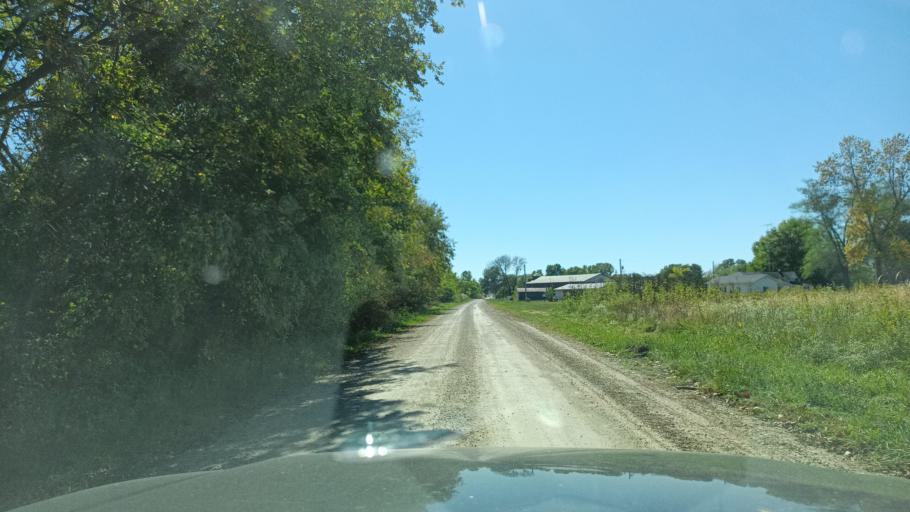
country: US
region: Missouri
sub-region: Macon County
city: La Plata
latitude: 39.9625
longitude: -92.6453
